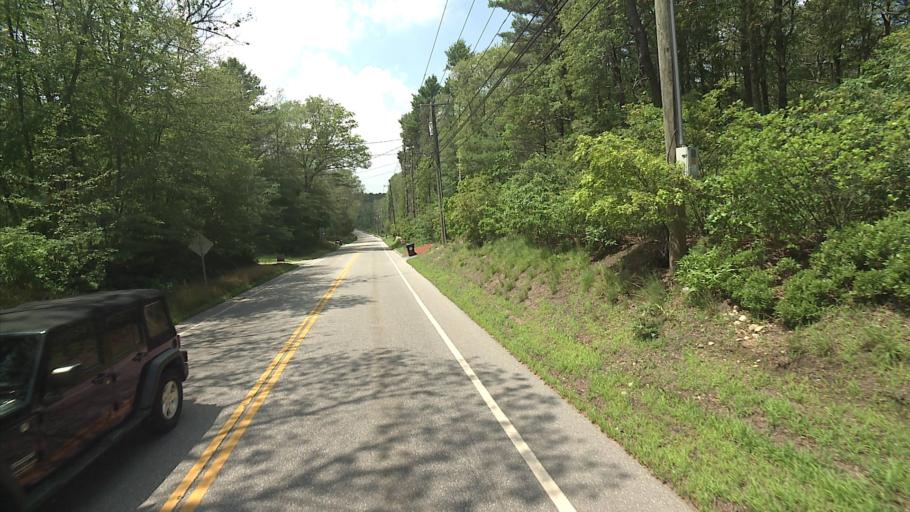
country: US
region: Rhode Island
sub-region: Washington County
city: Hopkinton
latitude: 41.5741
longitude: -71.8366
